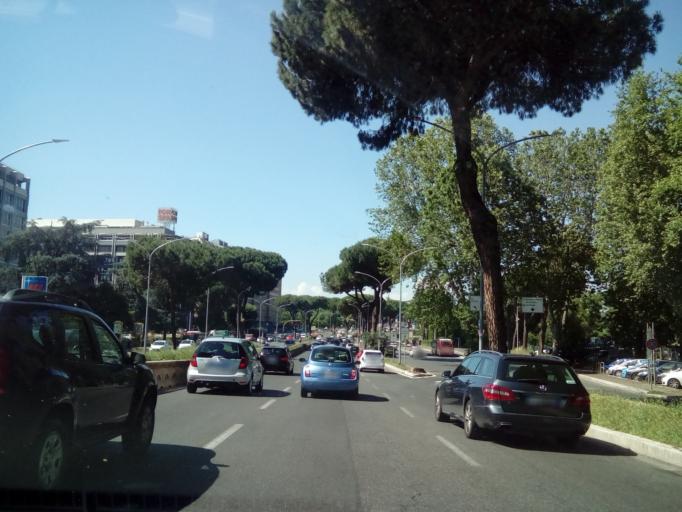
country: IT
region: Latium
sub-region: Citta metropolitana di Roma Capitale
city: Rome
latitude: 41.8657
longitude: 12.4970
